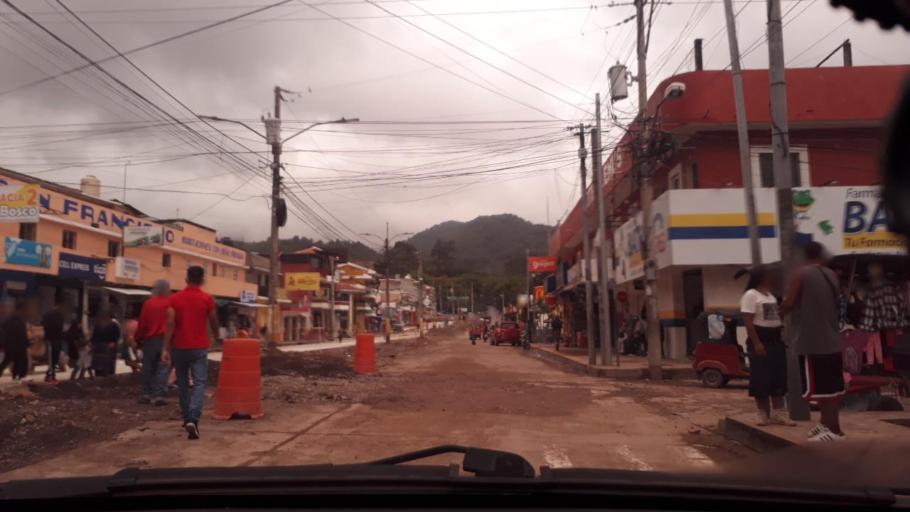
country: GT
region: Chiquimula
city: Esquipulas
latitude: 14.5632
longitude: -89.3520
